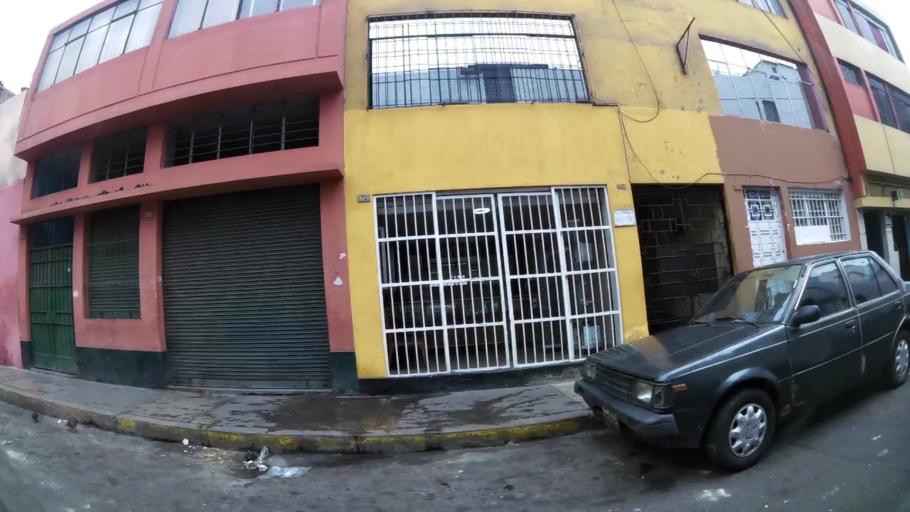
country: PE
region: Lima
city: Lima
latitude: -12.0450
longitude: -77.0406
